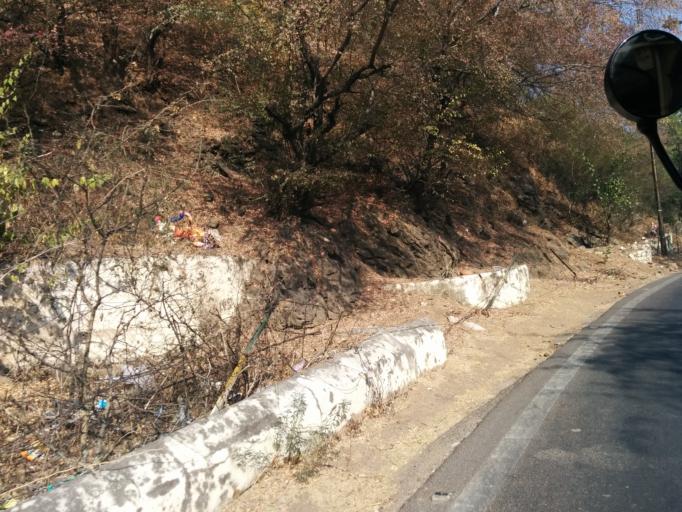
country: IN
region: Rajasthan
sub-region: Jaipur
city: Jaipur
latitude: 26.9681
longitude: 75.8482
